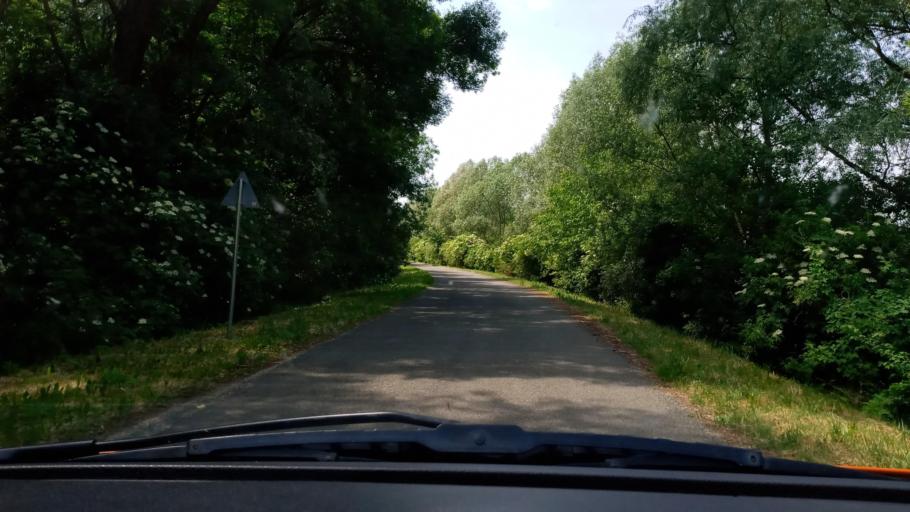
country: HU
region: Baranya
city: Sellye
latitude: 45.8076
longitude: 17.8786
